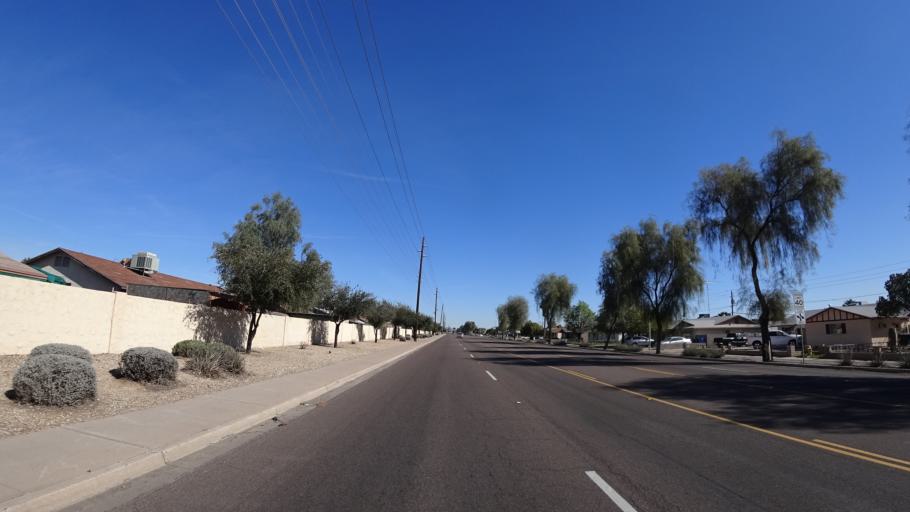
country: US
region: Arizona
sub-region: Maricopa County
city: Glendale
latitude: 33.5093
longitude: -112.2100
